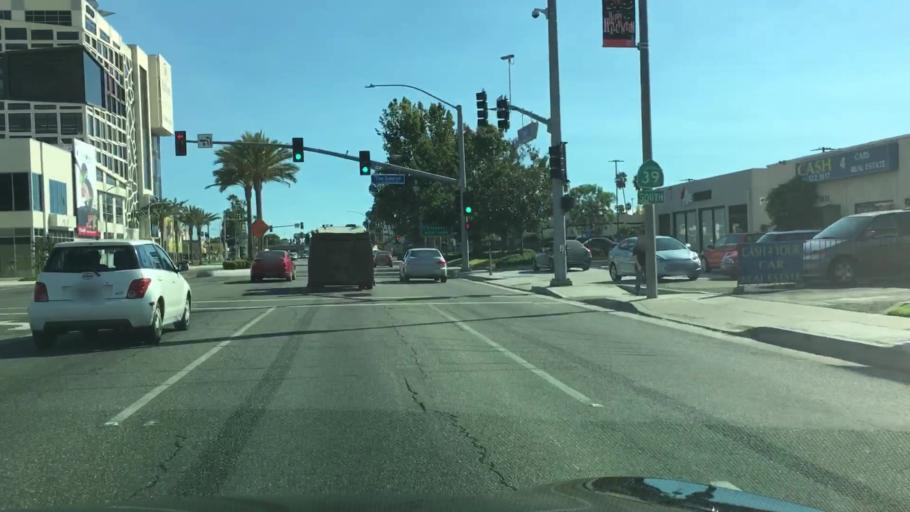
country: US
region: California
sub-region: Orange County
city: Buena Park
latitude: 33.8608
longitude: -117.9982
